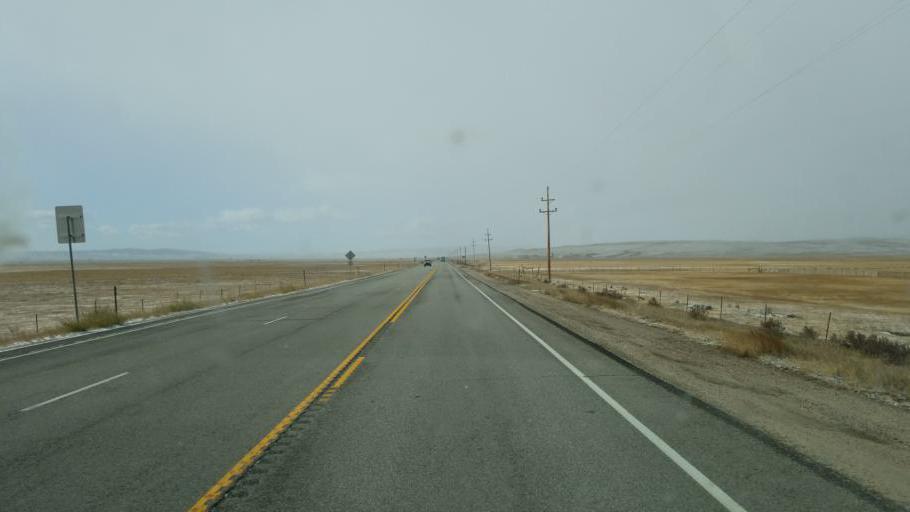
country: US
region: Colorado
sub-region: Summit County
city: Breckenridge
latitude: 39.4040
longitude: -105.7795
